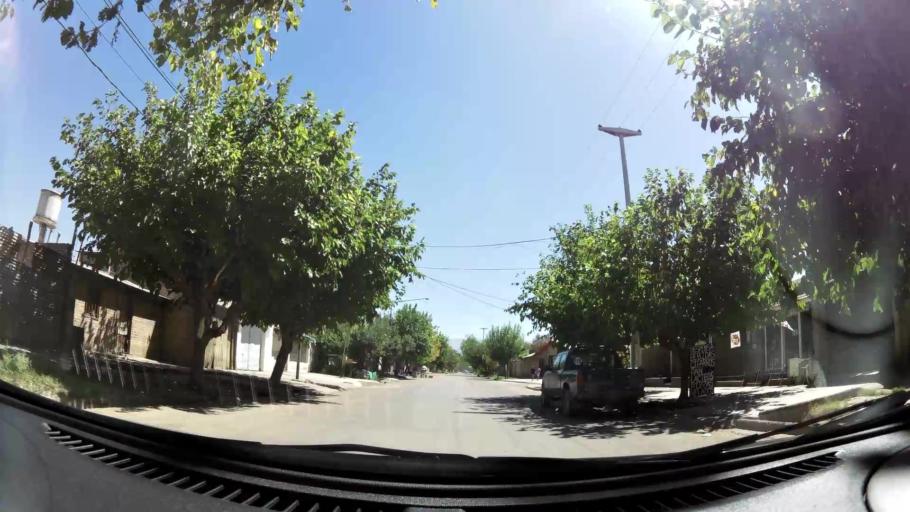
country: AR
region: Mendoza
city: Villa Nueva
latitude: -32.8797
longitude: -68.7930
